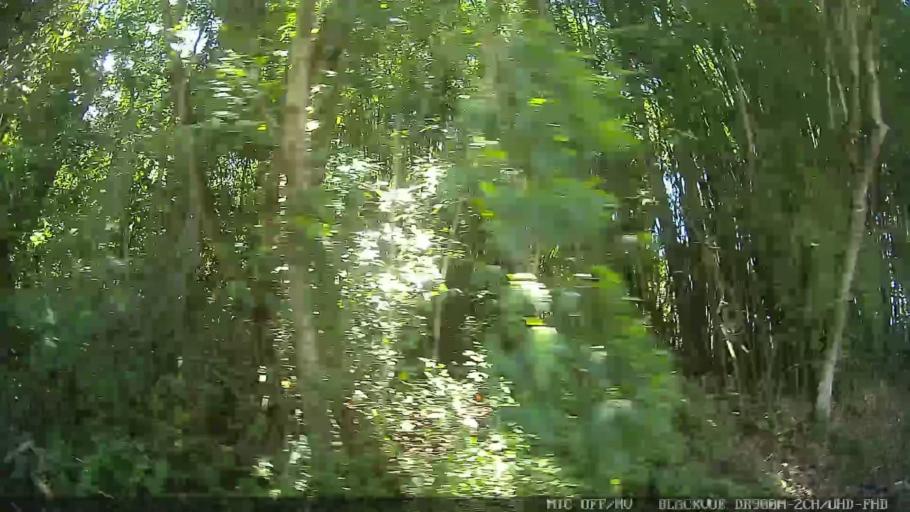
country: BR
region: Sao Paulo
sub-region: Mogi das Cruzes
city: Mogi das Cruzes
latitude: -23.5935
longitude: -46.1454
